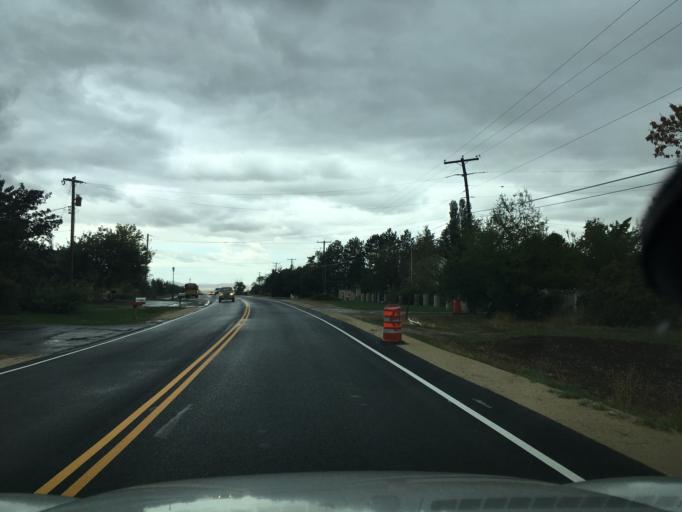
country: US
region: Utah
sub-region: Davis County
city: Fruit Heights
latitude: 41.0661
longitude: -111.9153
